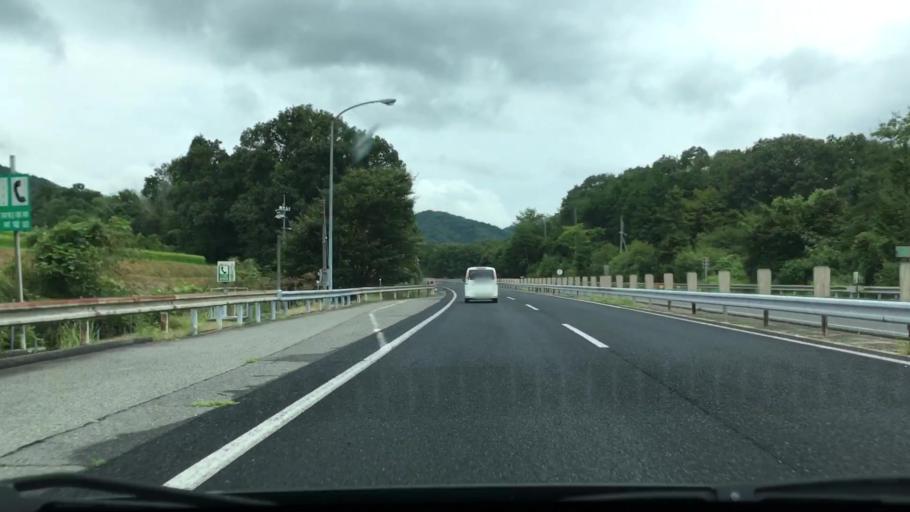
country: JP
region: Hiroshima
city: Miyoshi
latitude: 34.7241
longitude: 132.6908
